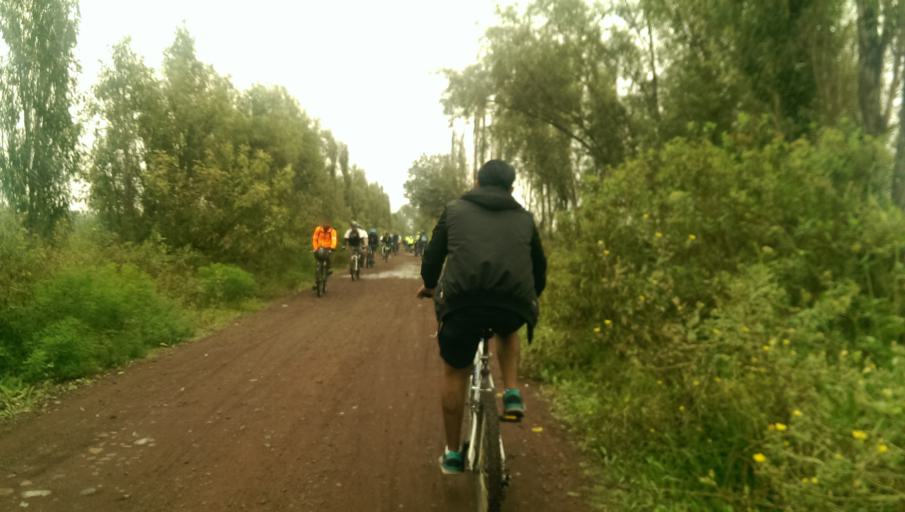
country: MX
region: Mexico City
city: Xochimilco
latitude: 19.2771
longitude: -99.0766
